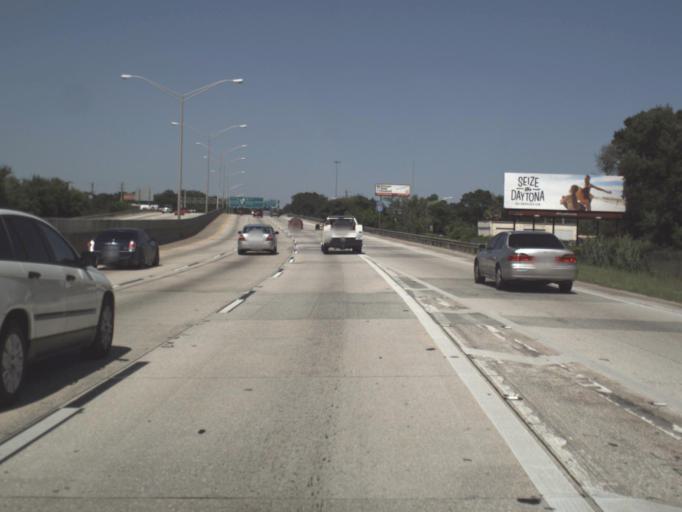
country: US
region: Florida
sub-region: Duval County
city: Jacksonville
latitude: 30.3178
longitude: -81.7281
